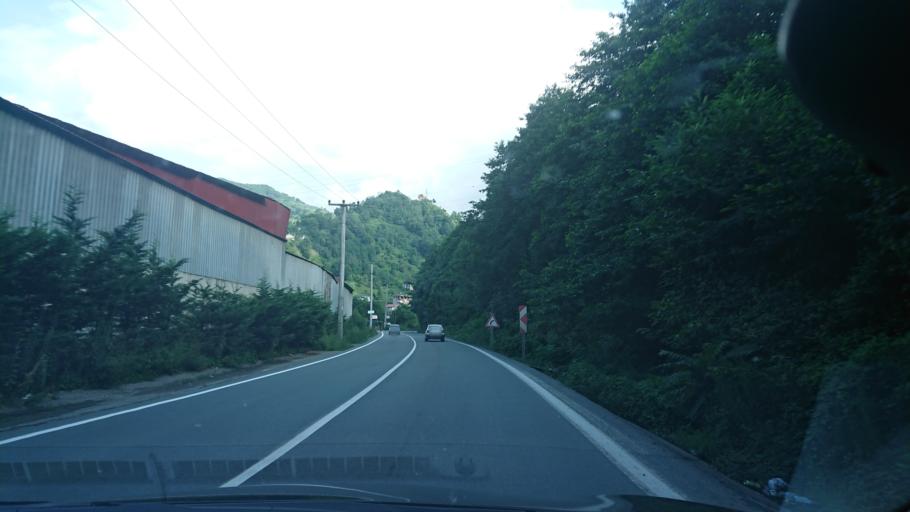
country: TR
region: Rize
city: Gundogdu
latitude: 41.0346
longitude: 40.5796
